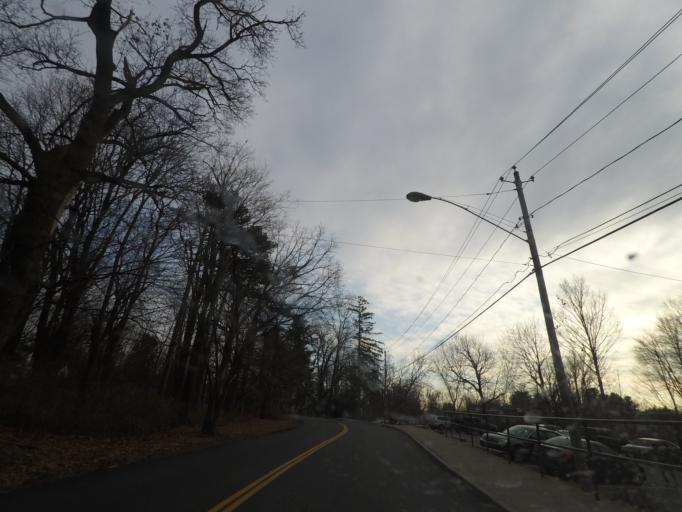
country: US
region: New York
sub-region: Rensselaer County
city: Troy
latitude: 42.7277
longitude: -73.6679
